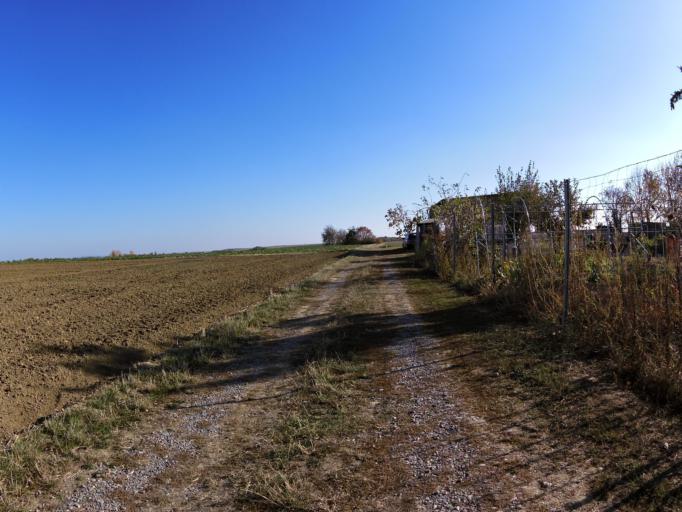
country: DE
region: Bavaria
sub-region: Regierungsbezirk Unterfranken
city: Eibelstadt
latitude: 49.7179
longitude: 9.9745
